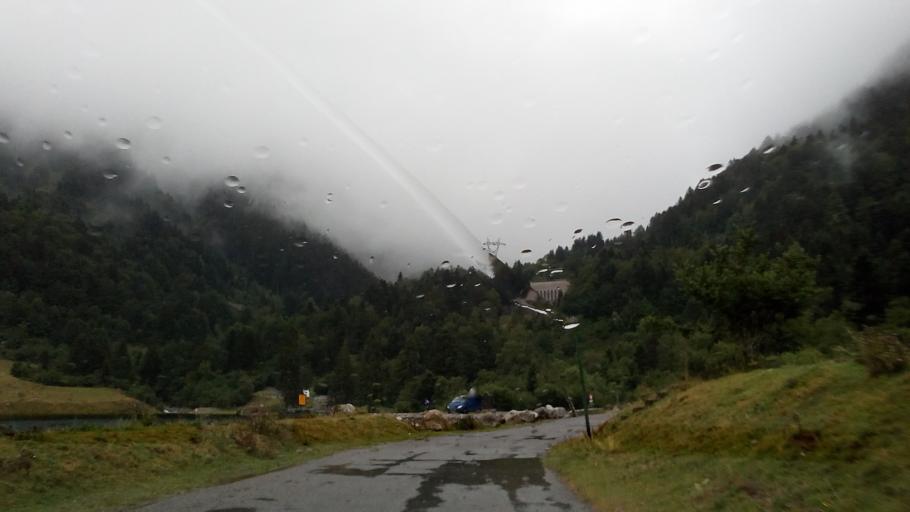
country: FR
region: Midi-Pyrenees
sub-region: Departement des Hautes-Pyrenees
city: Cauterets
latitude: 42.9136
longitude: -0.2590
